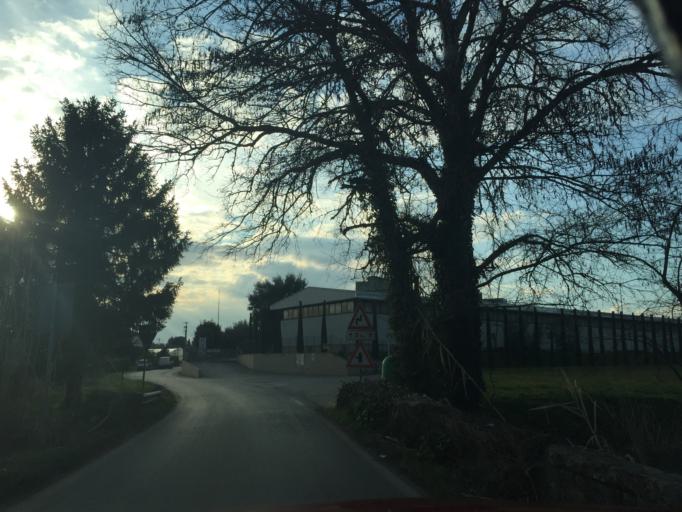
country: IT
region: Tuscany
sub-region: Provincia di Pistoia
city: San Rocco
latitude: 43.8414
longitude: 10.8658
